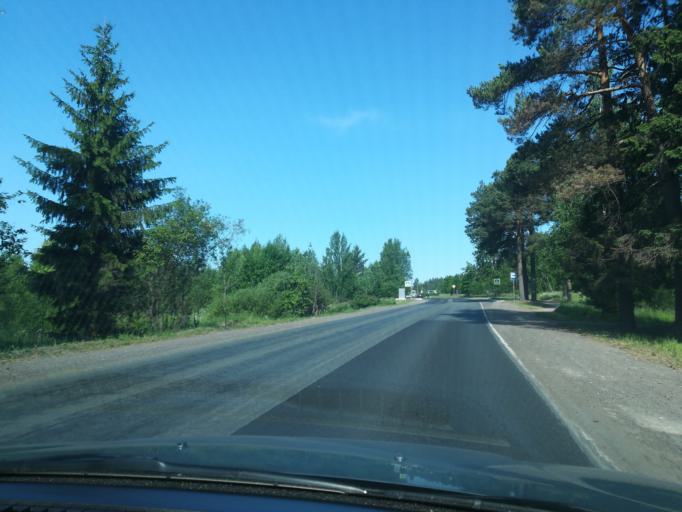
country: RU
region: Leningrad
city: Lesogorskiy
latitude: 61.0851
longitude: 28.9101
